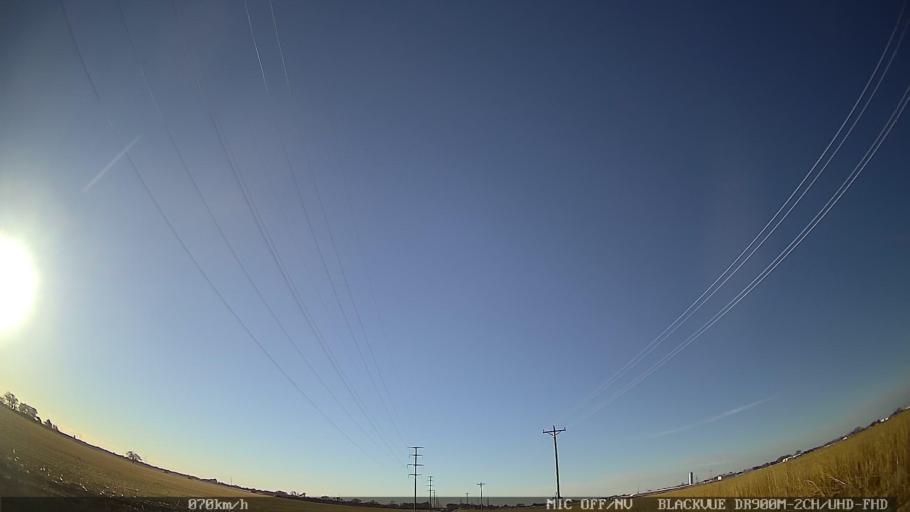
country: US
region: New Mexico
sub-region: Curry County
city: Clovis
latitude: 34.4218
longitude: -103.2493
